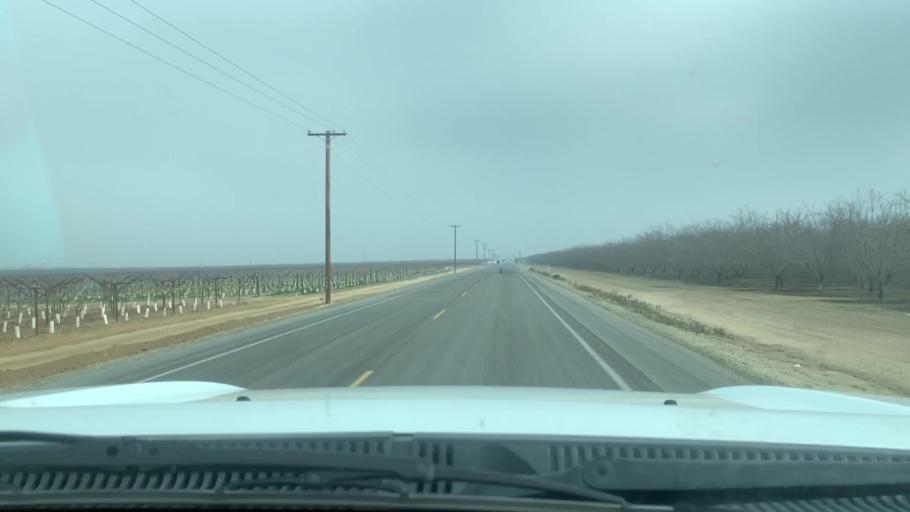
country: US
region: California
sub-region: Kern County
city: Buttonwillow
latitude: 35.5005
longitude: -119.4283
